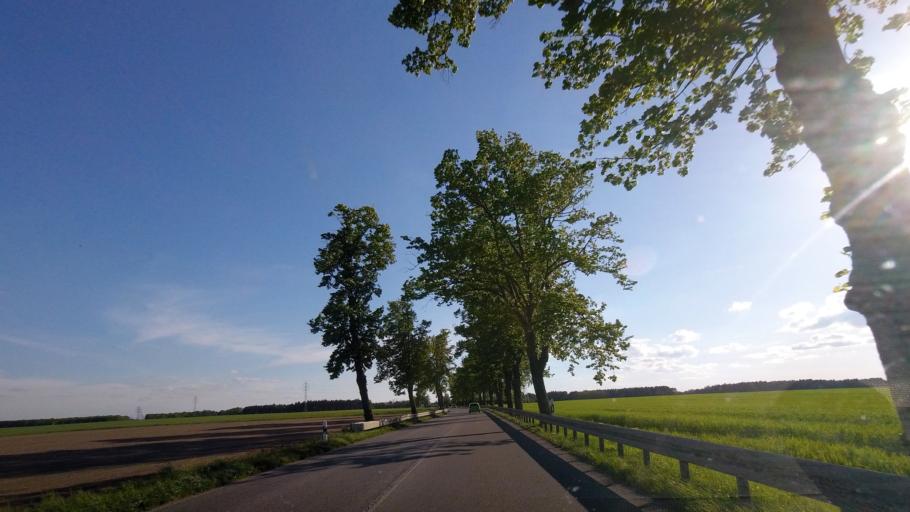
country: DE
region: Brandenburg
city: Luebben
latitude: 51.9272
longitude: 13.8785
